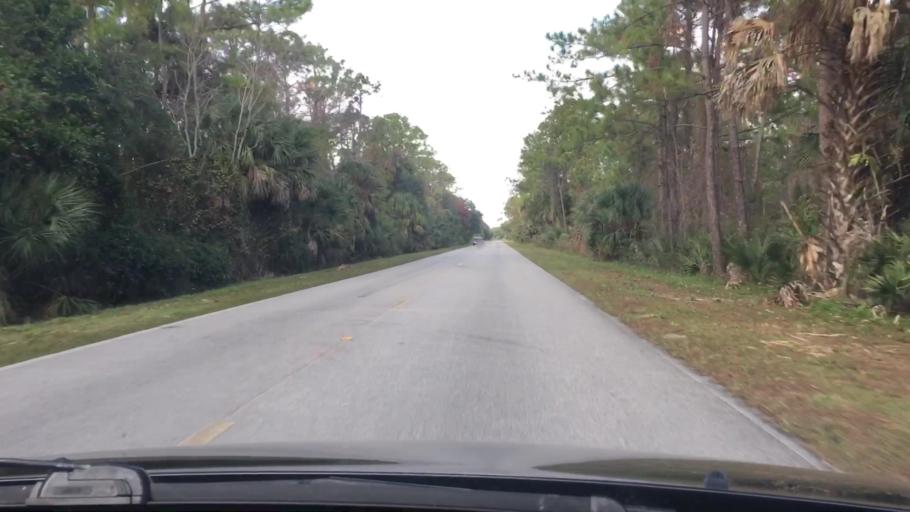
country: US
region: Florida
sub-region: Volusia County
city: Ormond Beach
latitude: 29.2923
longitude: -81.1277
